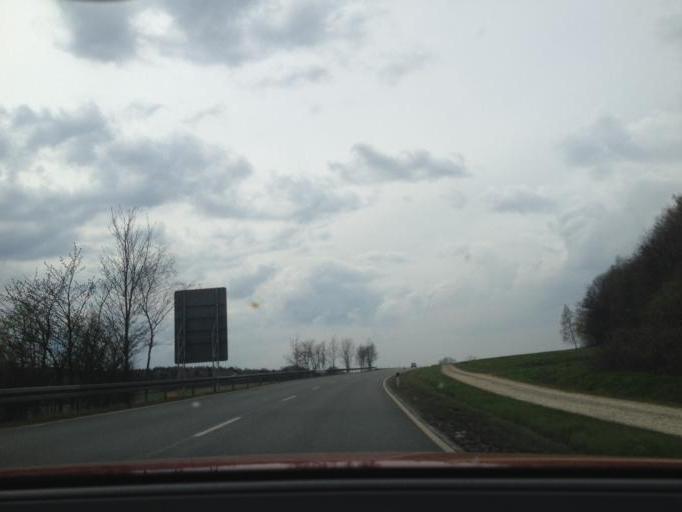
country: DE
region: Bavaria
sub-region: Upper Franconia
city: Bad Alexandersbad
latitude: 50.0226
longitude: 12.0124
